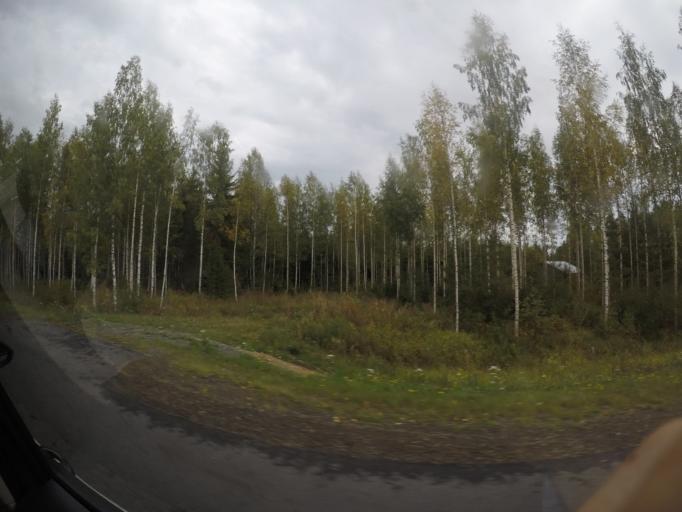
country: FI
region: Haeme
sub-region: Haemeenlinna
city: Parola
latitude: 61.1070
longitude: 24.4114
